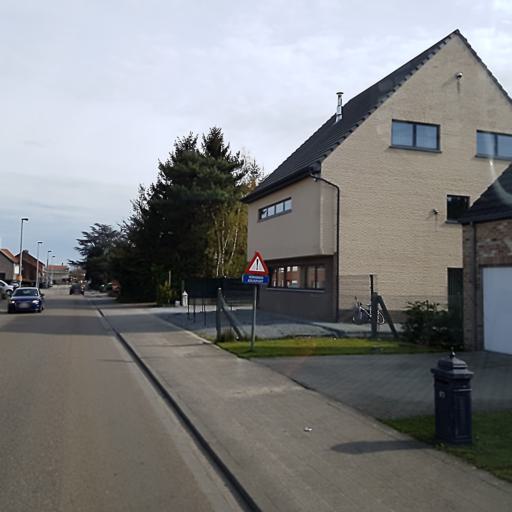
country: BE
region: Flanders
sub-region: Provincie Vlaams-Brabant
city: Aarschot
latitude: 51.0042
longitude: 4.8316
